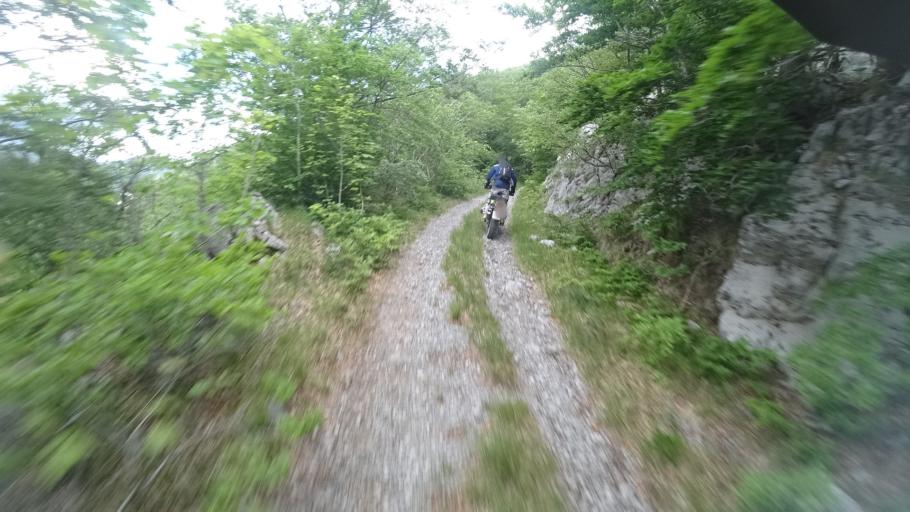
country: HR
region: Licko-Senjska
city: Gospic
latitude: 44.4323
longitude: 15.2877
